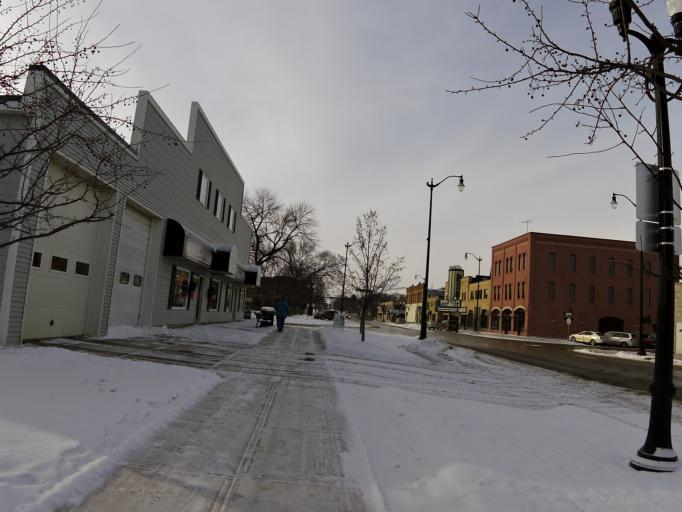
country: US
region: Minnesota
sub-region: McLeod County
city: Hutchinson
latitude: 44.8922
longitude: -94.3673
